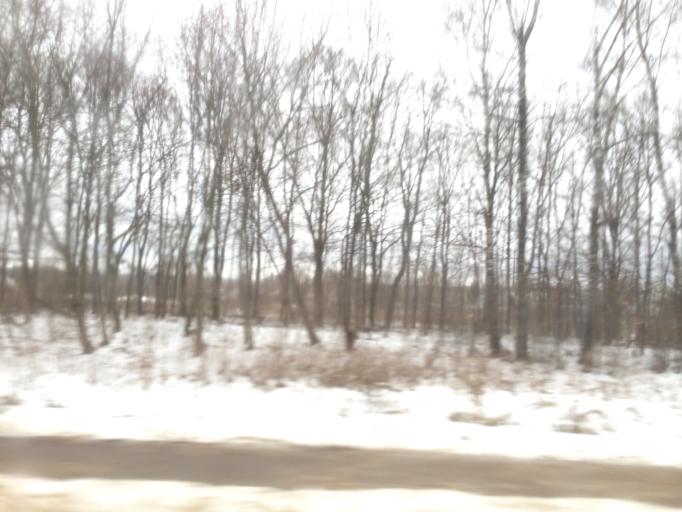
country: RU
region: Tula
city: Skuratovskiy
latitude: 54.1238
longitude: 37.6913
